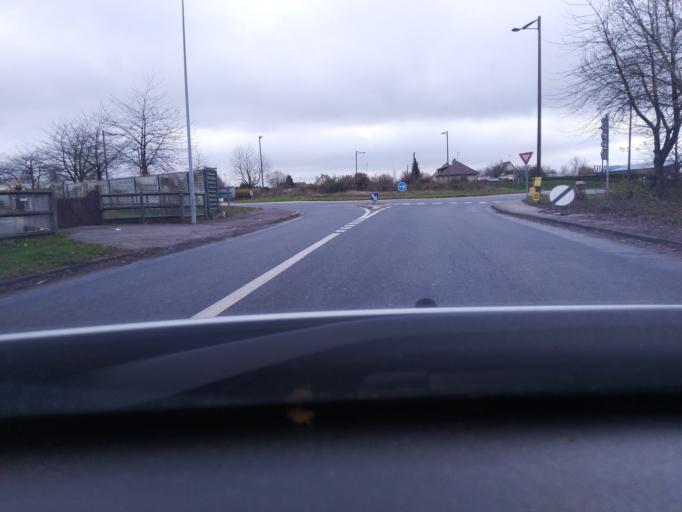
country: FR
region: Haute-Normandie
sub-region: Departement de la Seine-Maritime
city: Maromme
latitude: 49.4843
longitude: 1.0139
